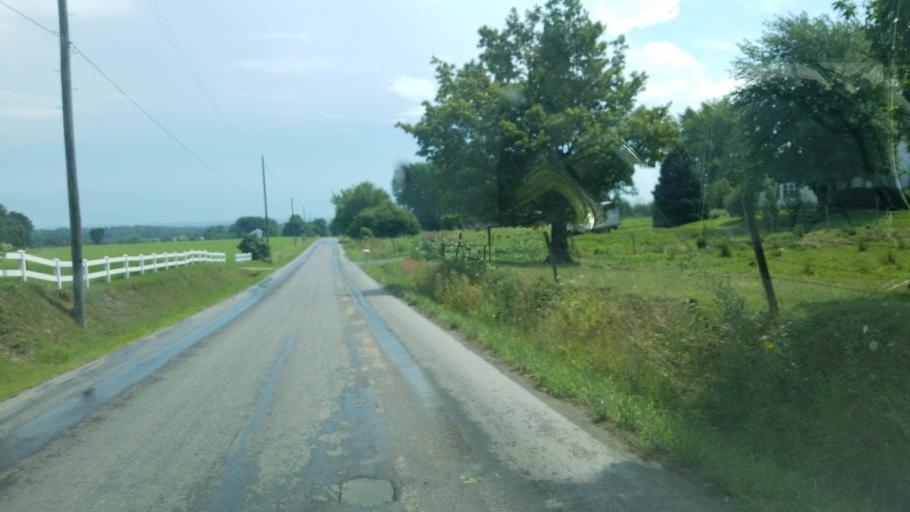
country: US
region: Ohio
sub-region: Geauga County
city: Middlefield
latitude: 41.4761
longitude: -81.0017
